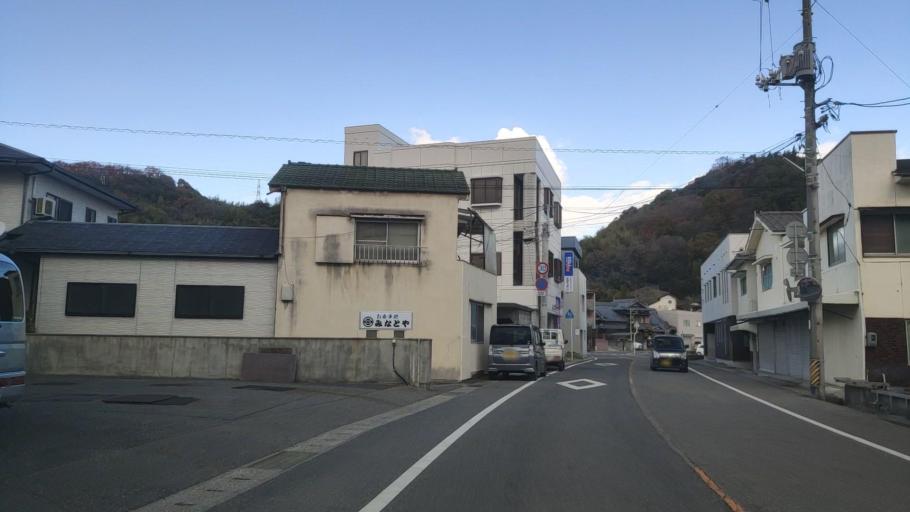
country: JP
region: Hiroshima
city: Innoshima
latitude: 34.2052
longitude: 133.1168
